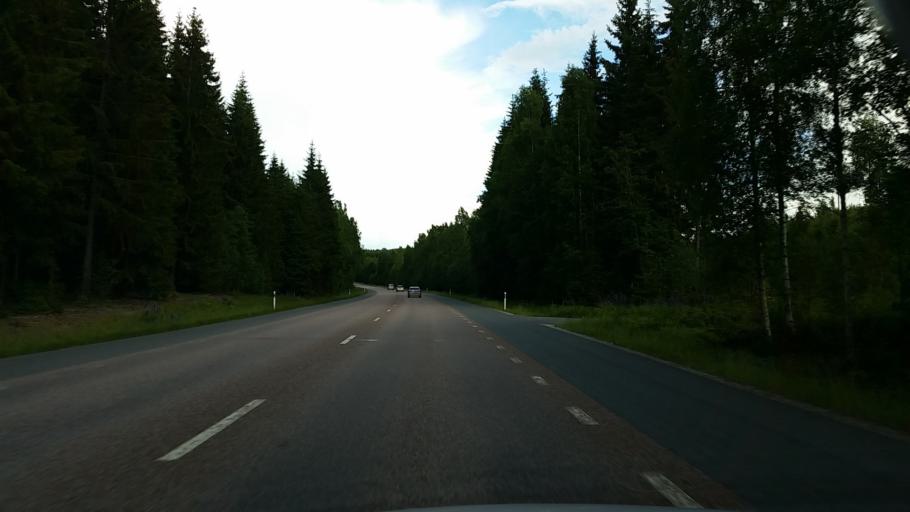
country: SE
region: Vaestmanland
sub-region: Fagersta Kommun
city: Fagersta
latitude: 59.9691
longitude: 15.7206
